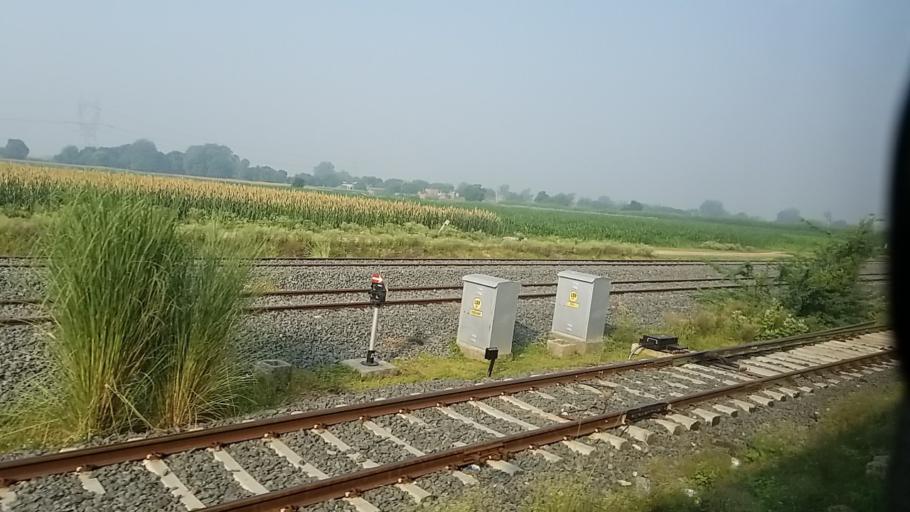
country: IN
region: Uttar Pradesh
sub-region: Firozabad
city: Sirsaganj
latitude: 26.9762
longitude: 78.7422
